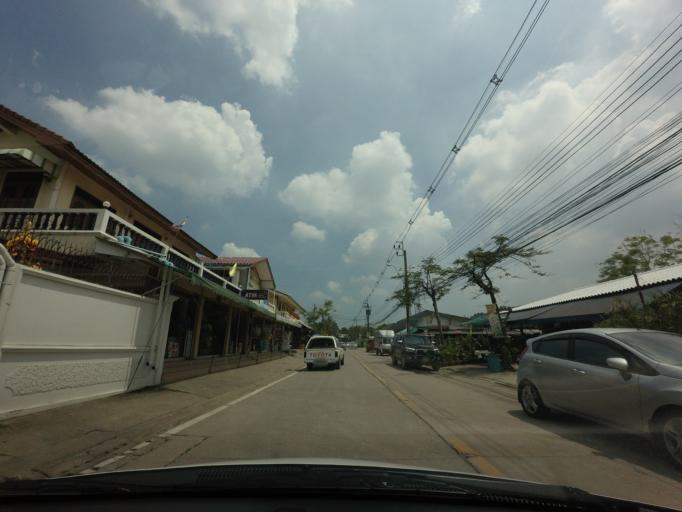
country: TH
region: Bangkok
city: Taling Chan
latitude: 13.7763
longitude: 100.4167
